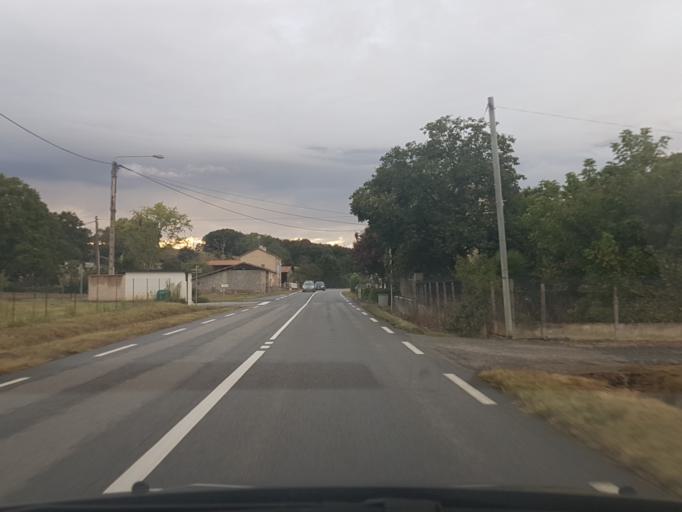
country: FR
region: Midi-Pyrenees
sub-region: Departement de l'Ariege
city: La Tour-du-Crieu
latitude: 43.0857
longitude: 1.7393
